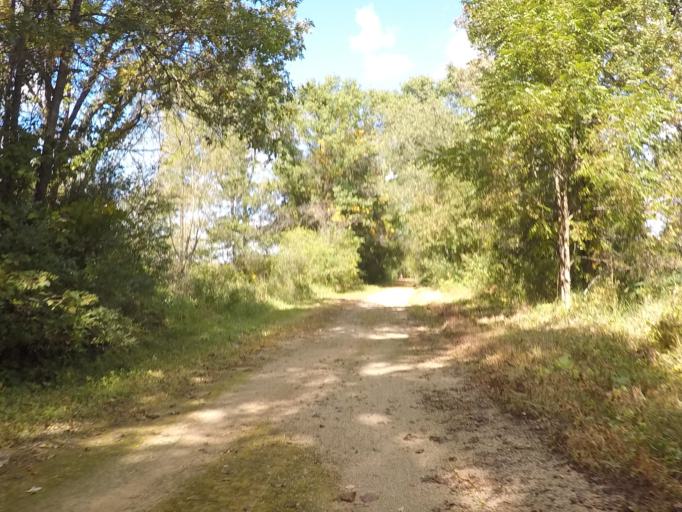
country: US
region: Wisconsin
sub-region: Richland County
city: Richland Center
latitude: 43.2888
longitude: -90.3237
